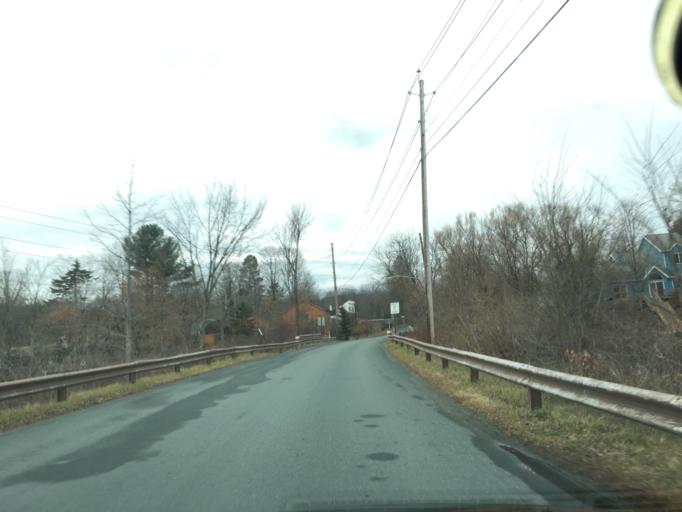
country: US
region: New York
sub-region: Rensselaer County
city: Averill Park
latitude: 42.6146
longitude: -73.5665
